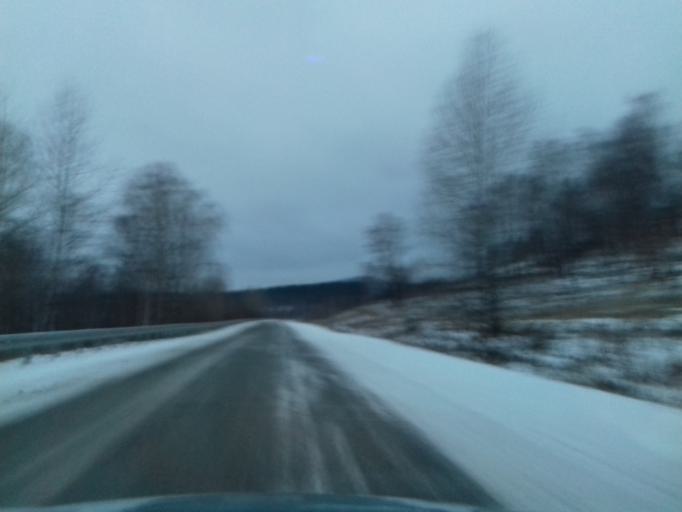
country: RU
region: Bashkortostan
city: Lomovka
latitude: 53.8646
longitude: 58.0558
